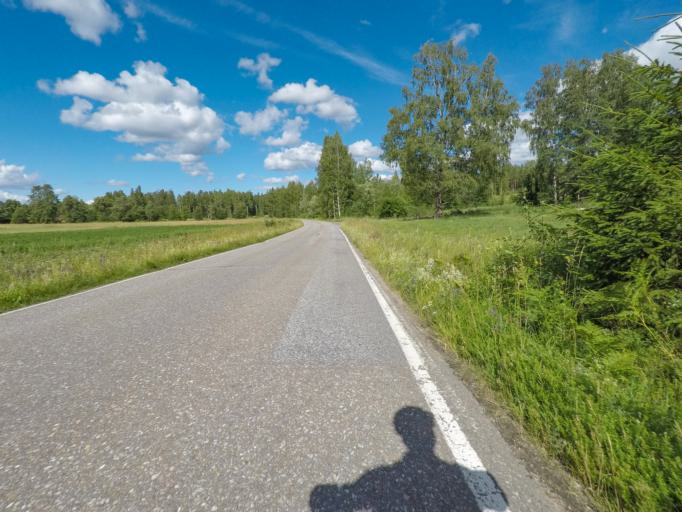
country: FI
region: South Karelia
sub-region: Lappeenranta
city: Joutseno
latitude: 61.1018
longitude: 28.3686
